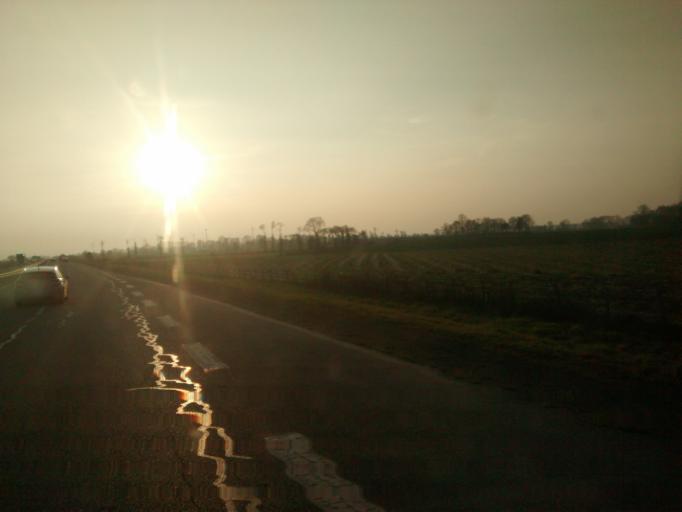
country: FR
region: Brittany
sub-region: Departement d'Ille-et-Vilaine
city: Maxent
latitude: 48.0303
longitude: -2.0181
